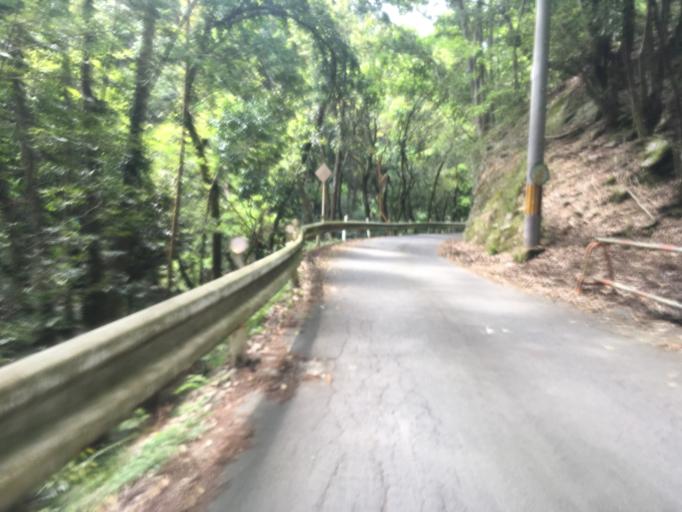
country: JP
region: Kyoto
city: Kameoka
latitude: 35.0316
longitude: 135.6344
